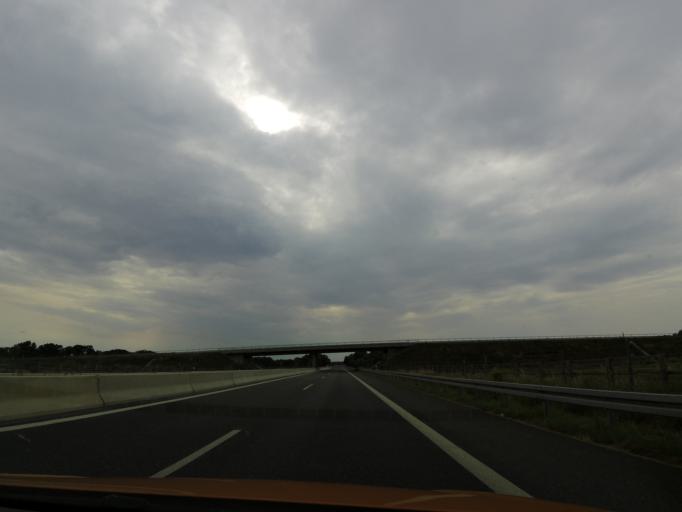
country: DE
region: Berlin
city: Lichtenrade
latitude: 52.3677
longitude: 13.3892
